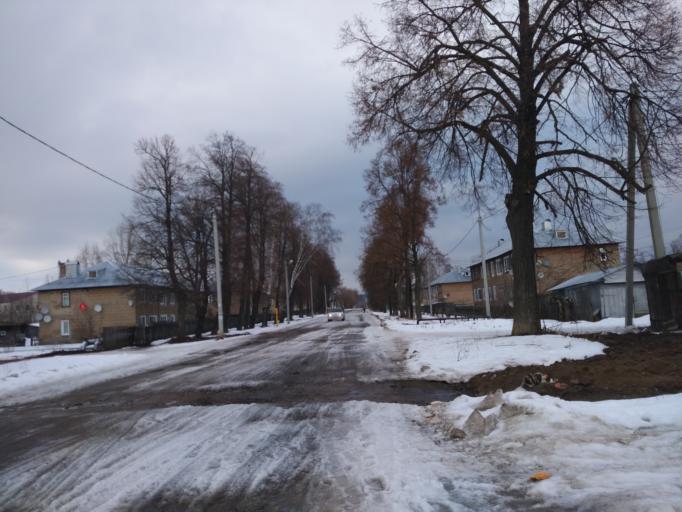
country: RU
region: Kirov
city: Krasnaya Polyana
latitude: 56.2396
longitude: 51.1414
